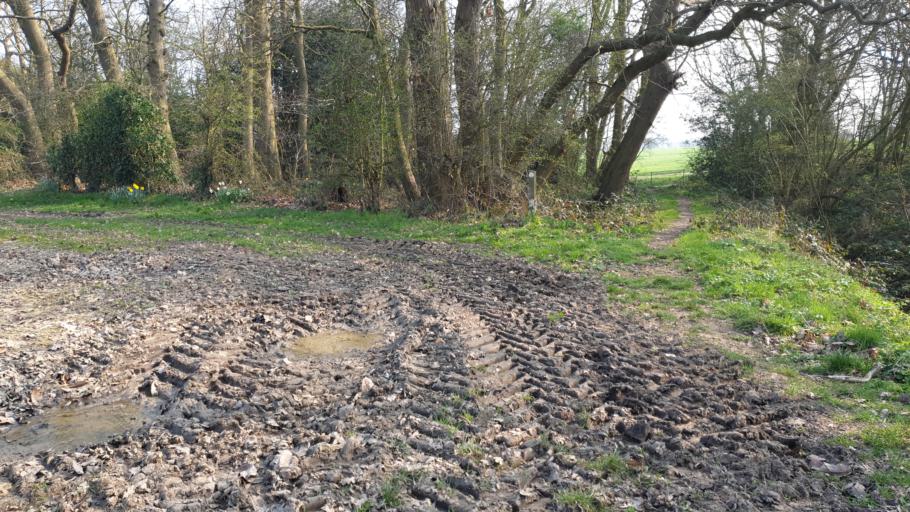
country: GB
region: England
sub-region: Essex
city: Great Bentley
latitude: 51.8852
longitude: 1.1190
